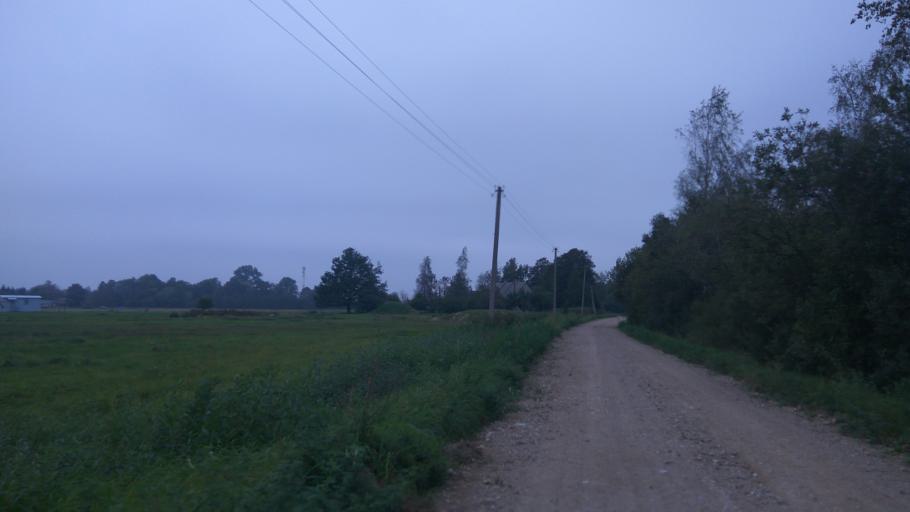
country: LV
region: Rucavas
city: Rucava
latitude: 56.1614
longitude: 21.1750
